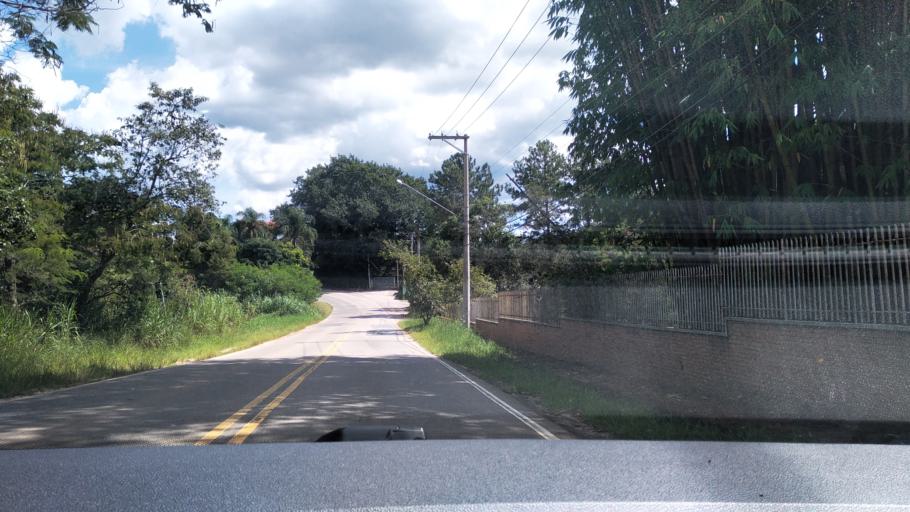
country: BR
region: Sao Paulo
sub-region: Varzea Paulista
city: Varzea Paulista
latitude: -23.2427
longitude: -46.8736
